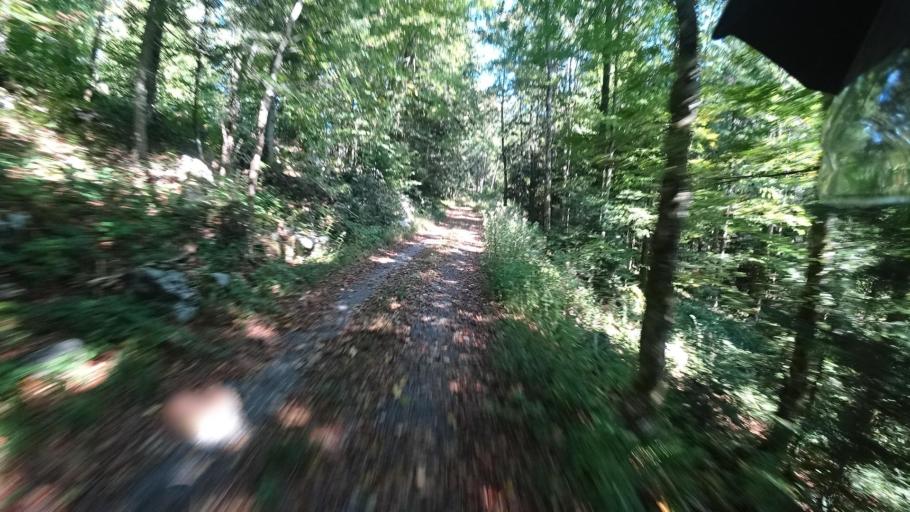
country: HR
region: Primorsko-Goranska
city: Vrbovsko
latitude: 45.2763
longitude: 15.1040
